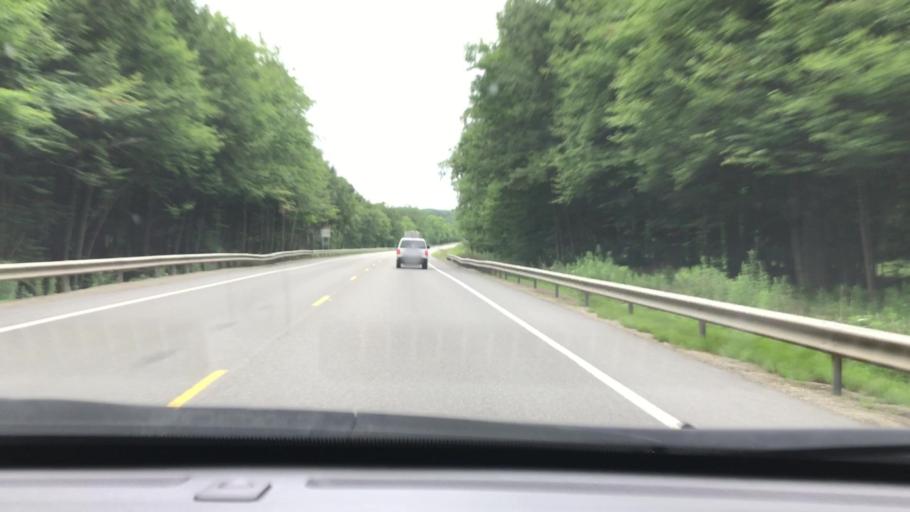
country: US
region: Pennsylvania
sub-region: McKean County
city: Kane
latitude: 41.6840
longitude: -78.6883
